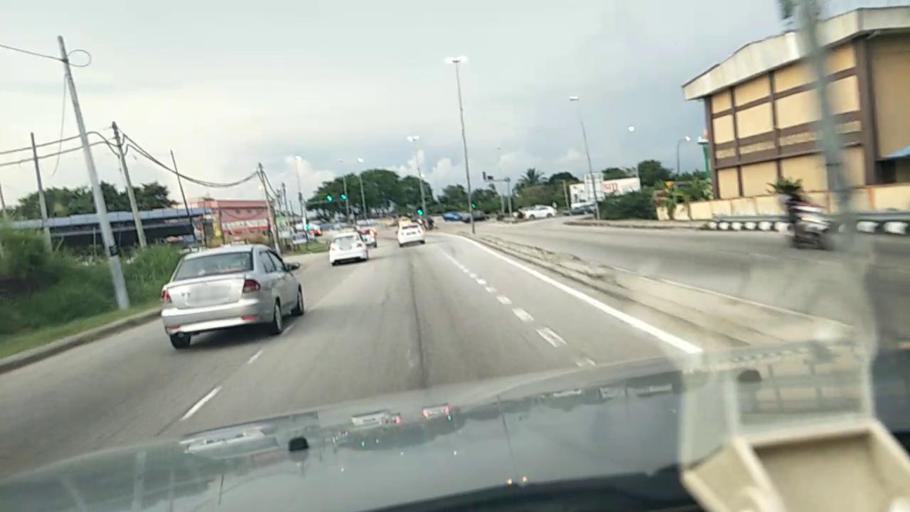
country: MY
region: Perak
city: Kampong Dungun
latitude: 3.1350
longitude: 101.3759
